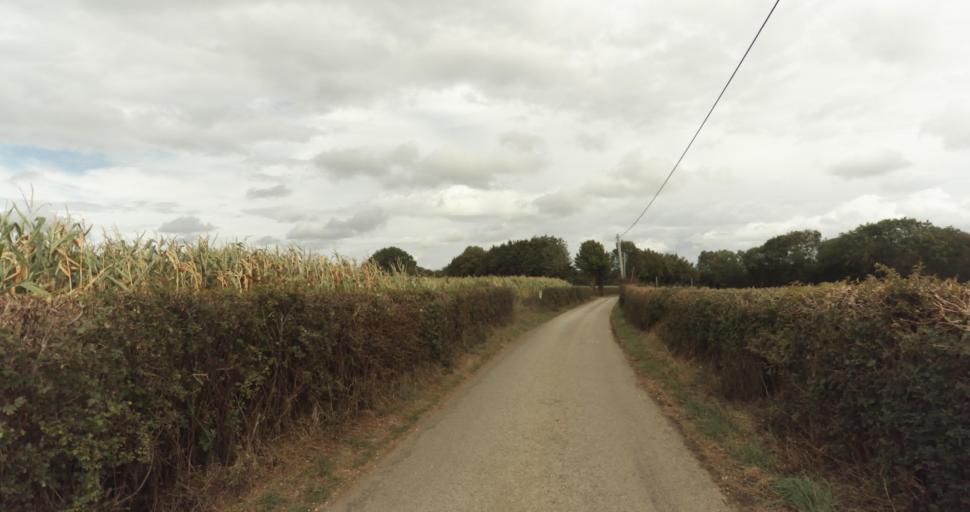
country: FR
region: Lower Normandy
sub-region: Departement de l'Orne
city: Gace
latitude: 48.8518
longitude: 0.2592
